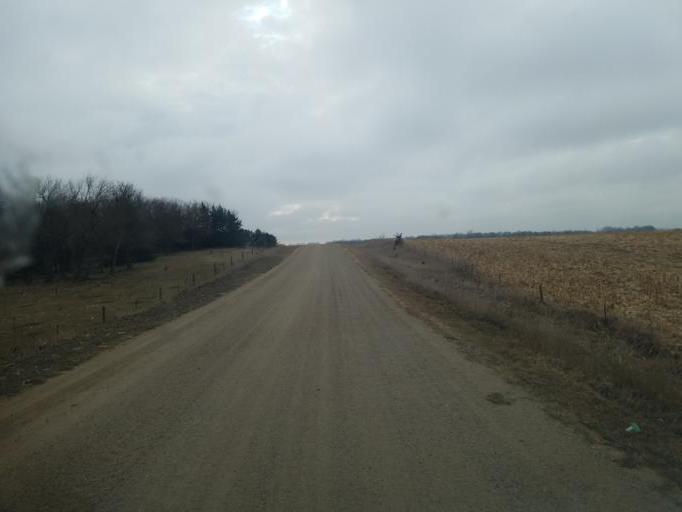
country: US
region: Nebraska
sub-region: Knox County
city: Creighton
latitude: 42.4664
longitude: -97.7984
